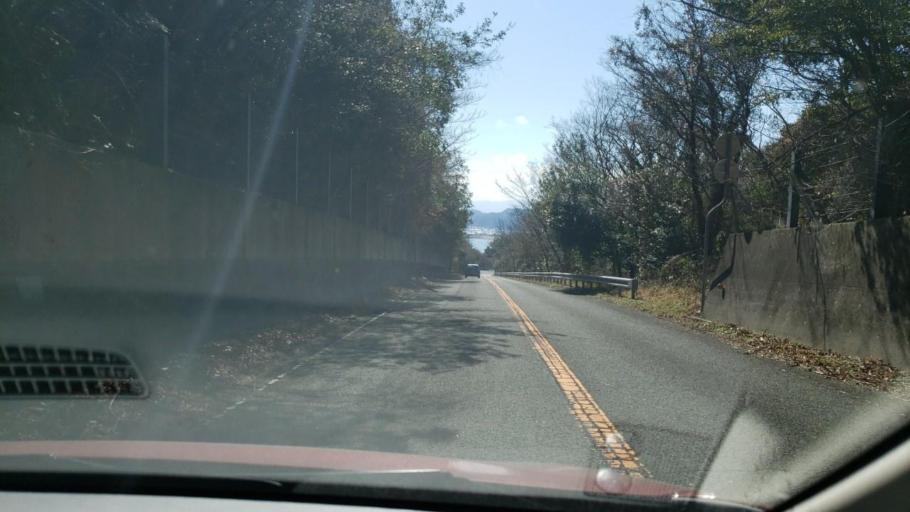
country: JP
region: Tokushima
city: Narutocho-mitsuishi
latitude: 34.2372
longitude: 134.6060
